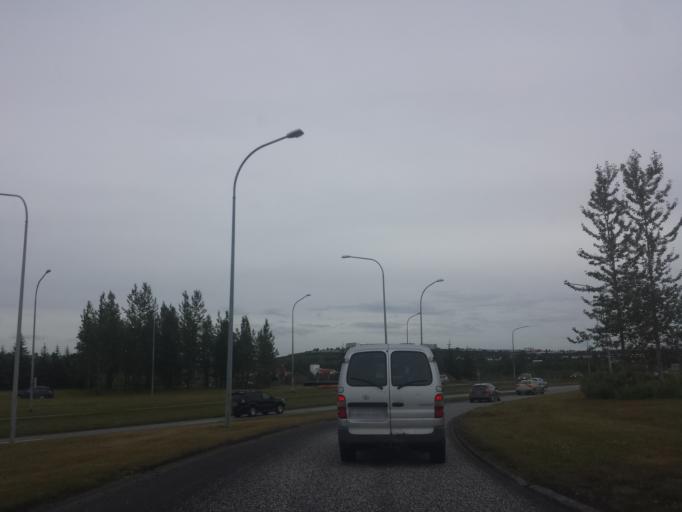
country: IS
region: Capital Region
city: Reykjavik
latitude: 64.1231
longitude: -21.8487
